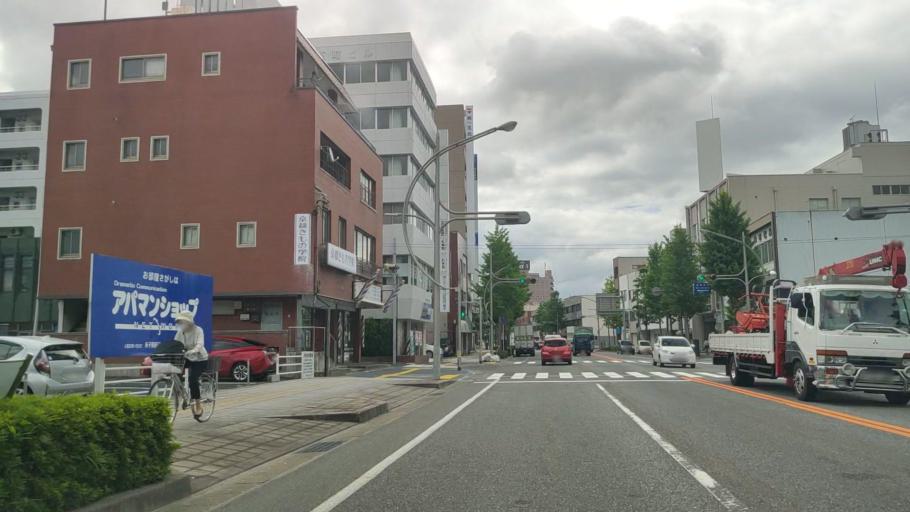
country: JP
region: Tottori
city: Yonago
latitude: 35.4266
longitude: 133.3303
